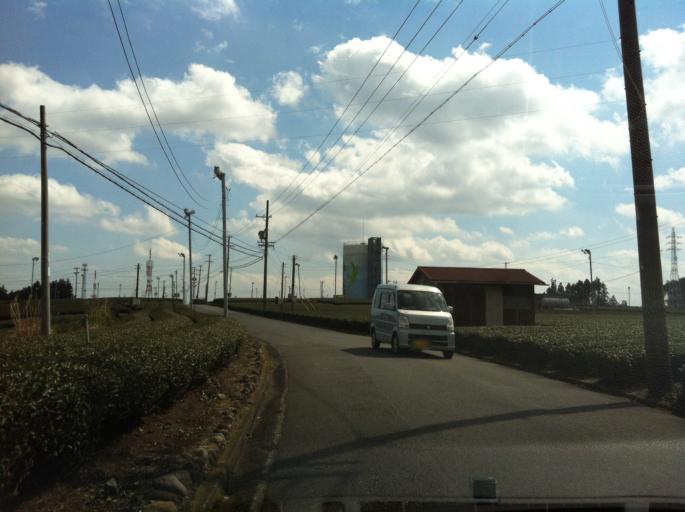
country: JP
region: Shizuoka
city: Kanaya
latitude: 34.8138
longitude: 138.1226
